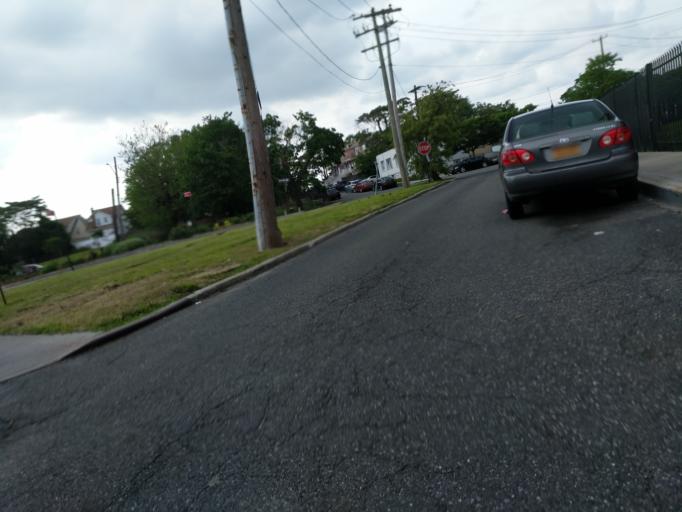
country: US
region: New York
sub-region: Nassau County
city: Inwood
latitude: 40.5955
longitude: -73.7574
